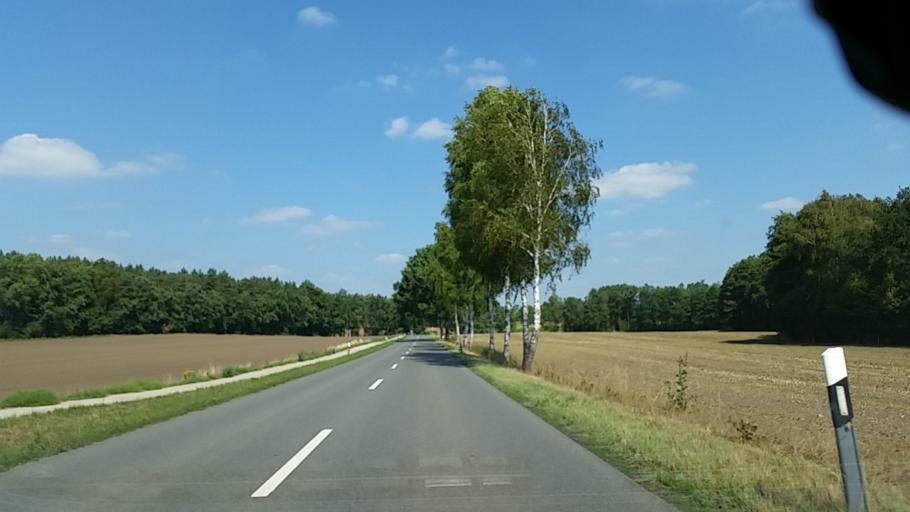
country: DE
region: Lower Saxony
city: Bienenbuttel
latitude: 53.1513
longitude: 10.4948
